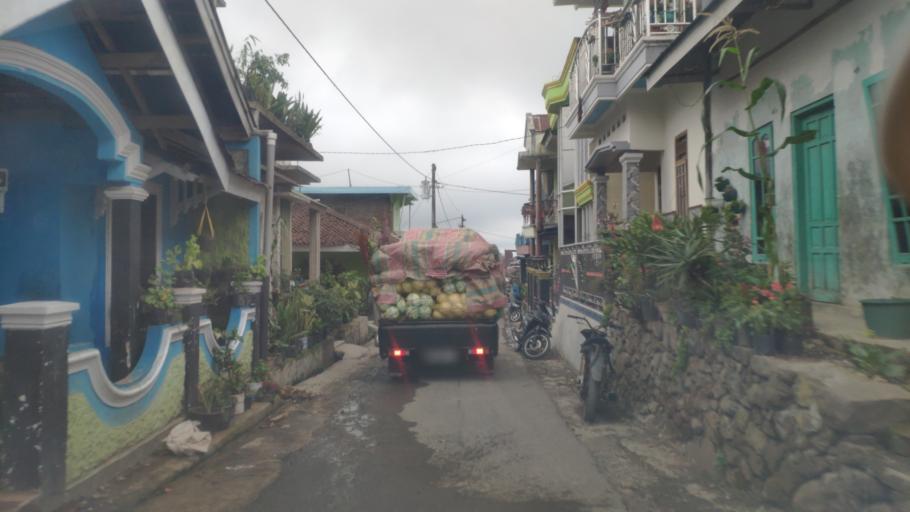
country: ID
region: Central Java
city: Wonosobo
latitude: -7.2319
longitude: 109.7165
